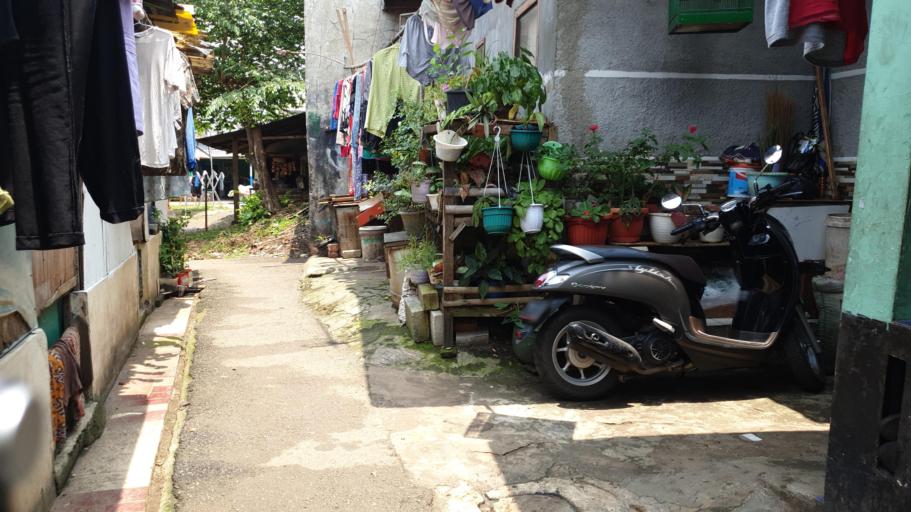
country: ID
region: West Java
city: Pamulang
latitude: -6.3004
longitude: 106.7778
